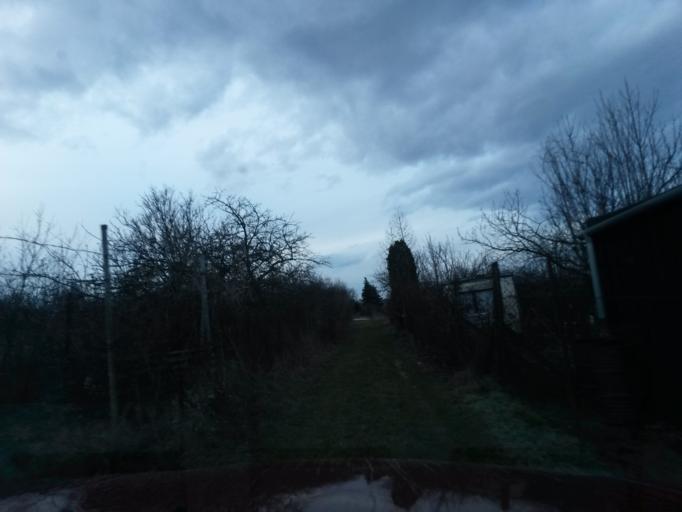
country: SK
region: Kosicky
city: Kosice
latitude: 48.7272
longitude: 21.3081
